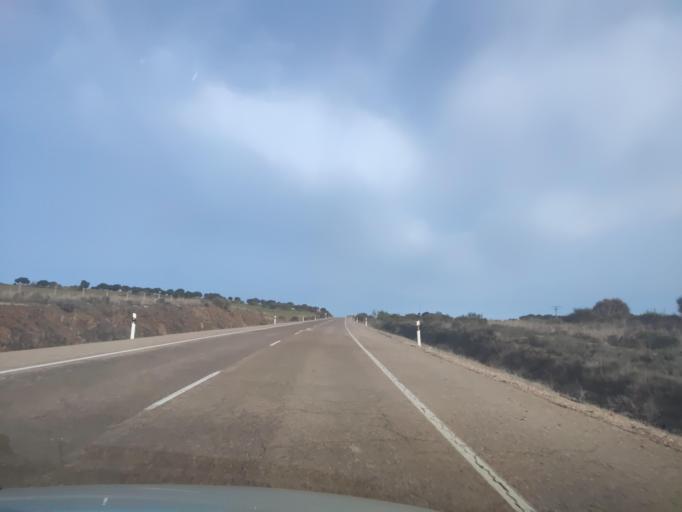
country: ES
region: Castille and Leon
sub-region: Provincia de Salamanca
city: Carpio de Azaba
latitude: 40.5912
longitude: -6.6675
